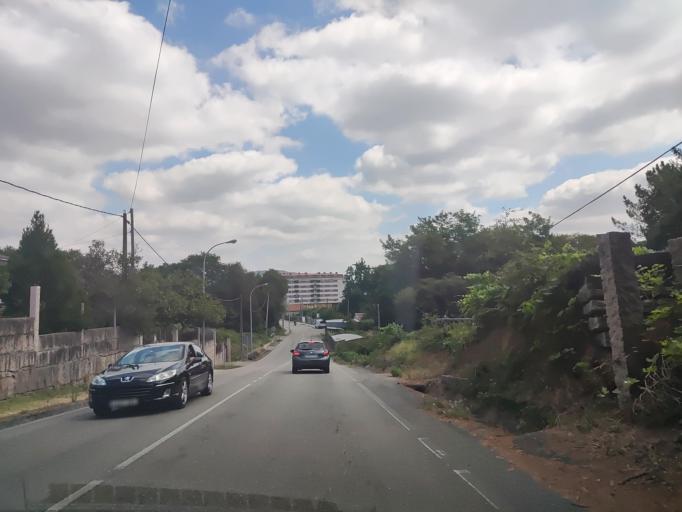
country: ES
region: Galicia
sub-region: Provincia de Pontevedra
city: Porrino
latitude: 42.1504
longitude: -8.6376
